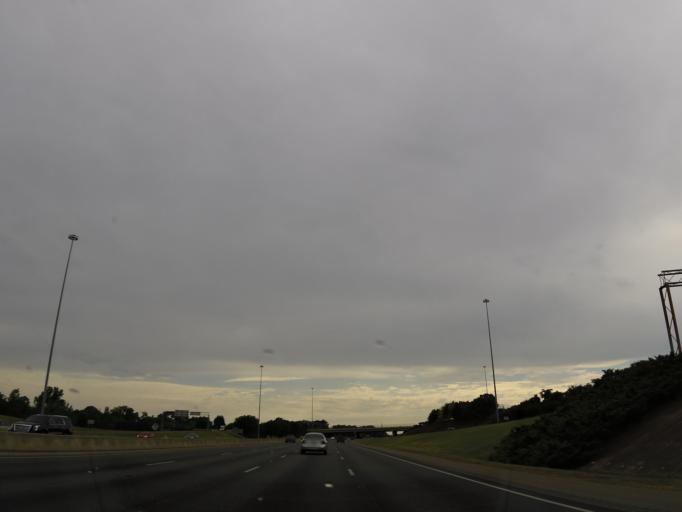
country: US
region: Alabama
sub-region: Madison County
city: Huntsville
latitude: 34.7213
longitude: -86.6228
